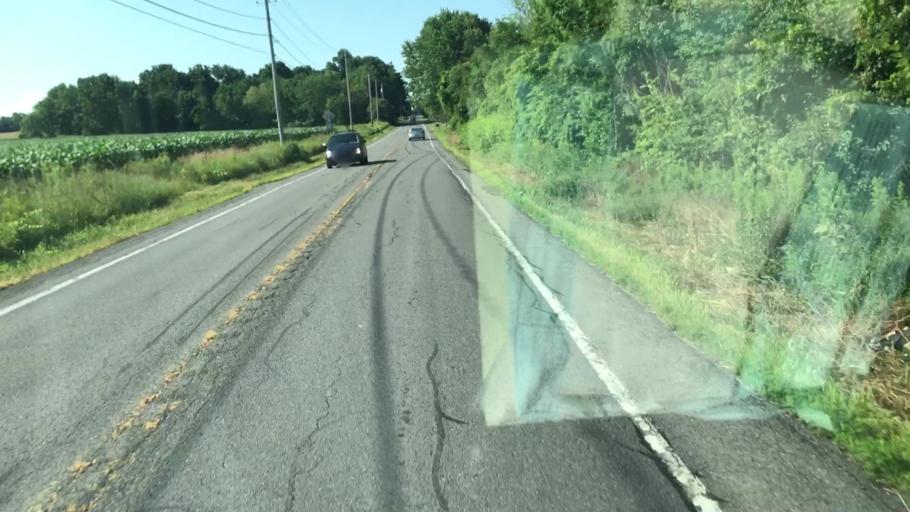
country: US
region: New York
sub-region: Onondaga County
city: Skaneateles
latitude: 42.9902
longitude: -76.4290
